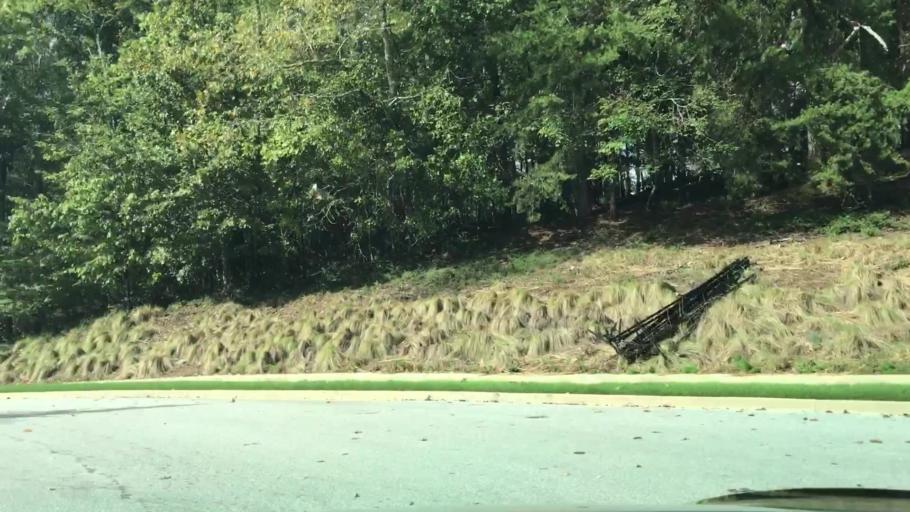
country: US
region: Georgia
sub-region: Gwinnett County
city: Buford
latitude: 34.1793
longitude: -84.0324
